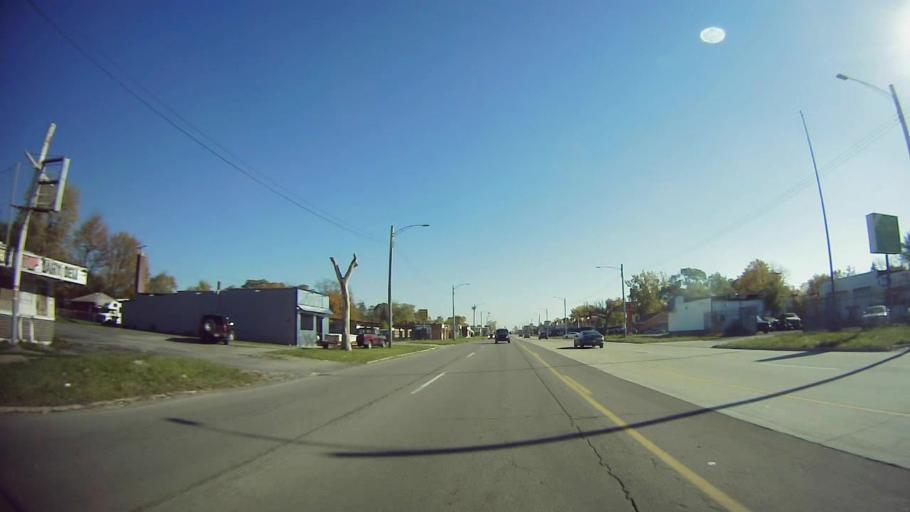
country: US
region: Michigan
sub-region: Wayne County
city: Dearborn Heights
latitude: 42.3574
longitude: -83.2438
